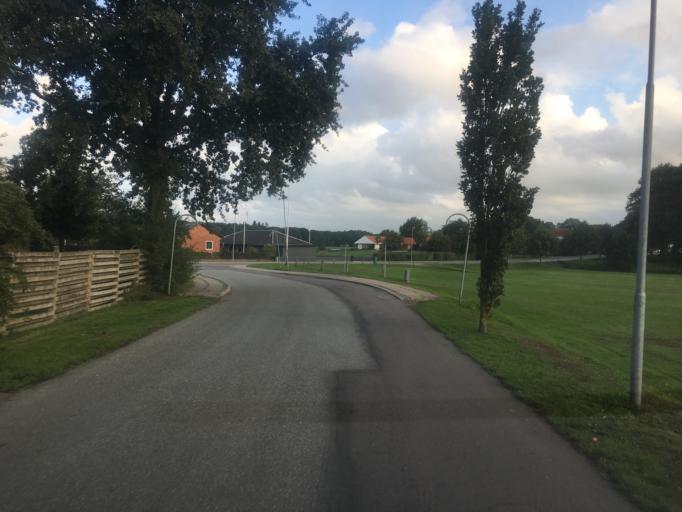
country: DK
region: South Denmark
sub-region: Tonder Kommune
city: Logumkloster
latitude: 55.0553
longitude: 8.9480
